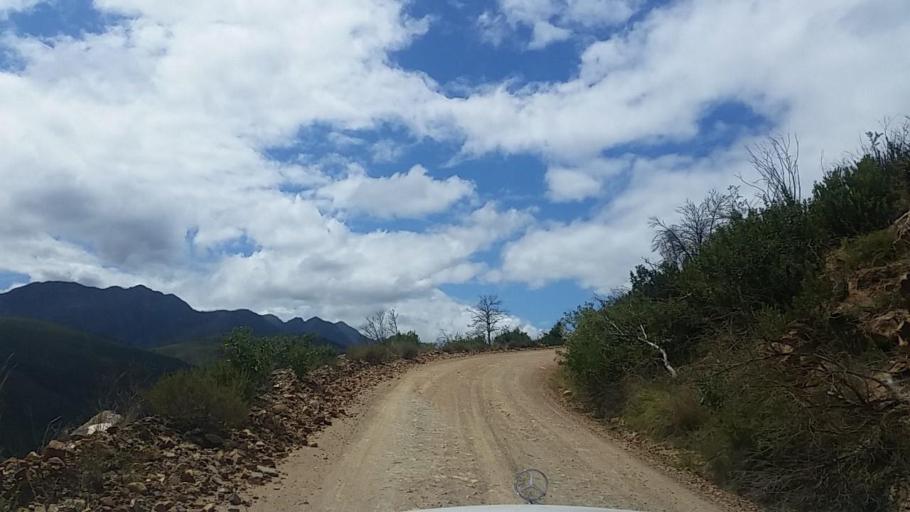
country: ZA
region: Western Cape
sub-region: Eden District Municipality
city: Knysna
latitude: -33.8262
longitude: 23.1844
